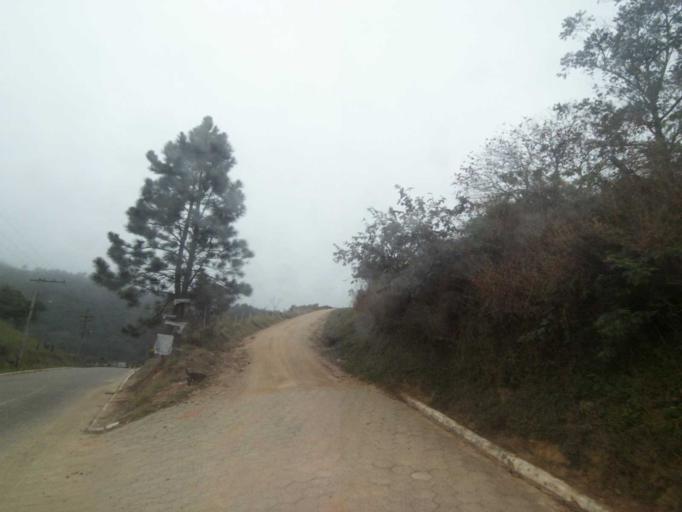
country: BR
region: Santa Catarina
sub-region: Anitapolis
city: Anitapolis
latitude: -27.9086
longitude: -49.1311
